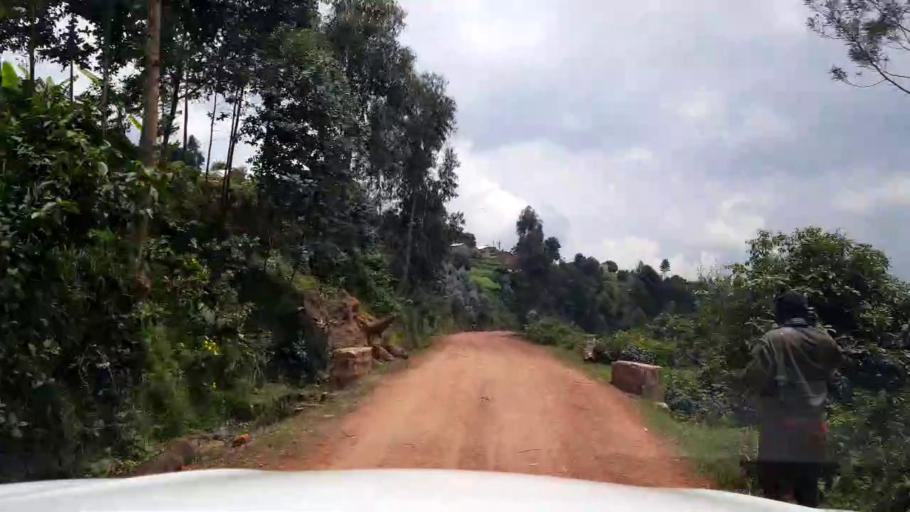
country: RW
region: Northern Province
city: Byumba
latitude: -1.4935
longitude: 29.9323
